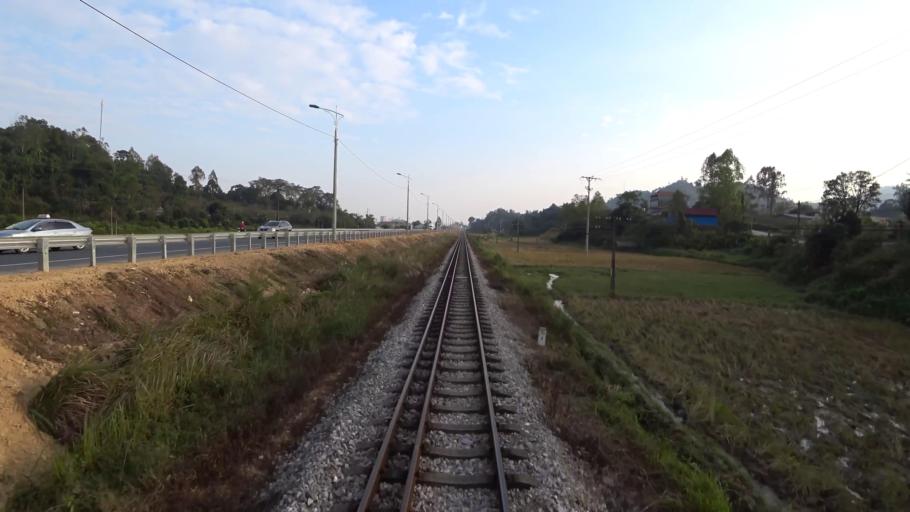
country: VN
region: Lang Son
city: Thi Tran Cao Loc
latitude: 21.8988
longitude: 106.7407
